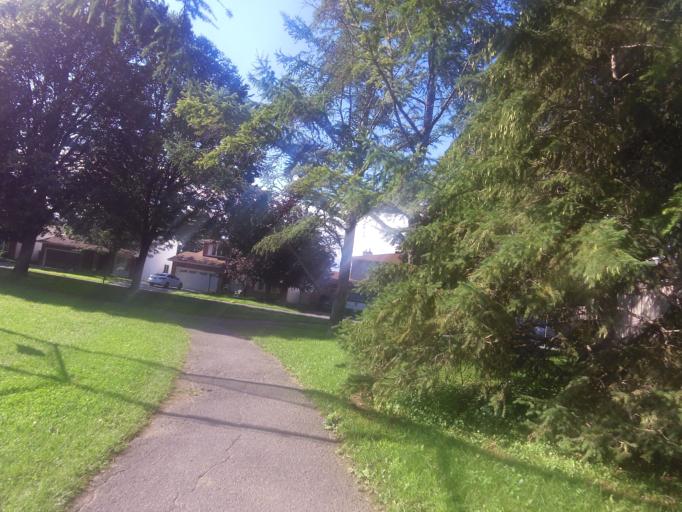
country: CA
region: Ontario
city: Ottawa
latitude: 45.3362
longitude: -75.7435
